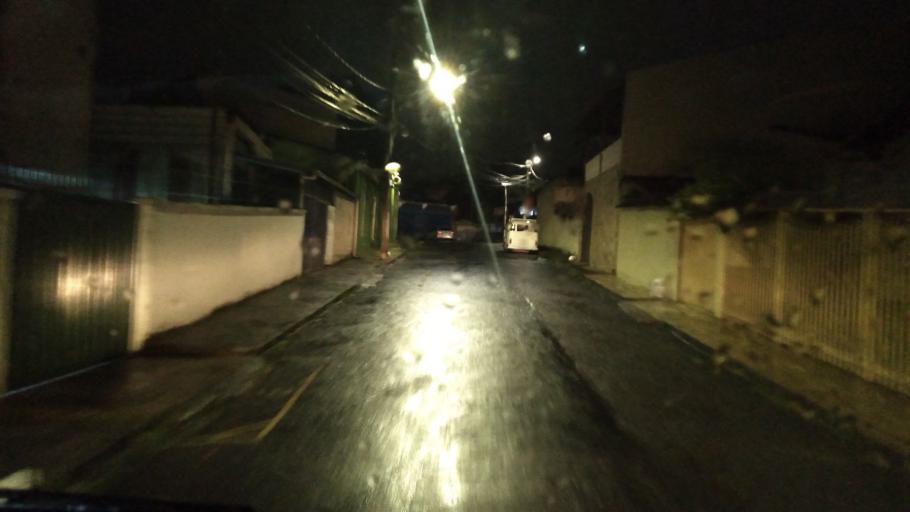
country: BR
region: Minas Gerais
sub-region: Belo Horizonte
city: Belo Horizonte
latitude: -19.9070
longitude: -43.9801
